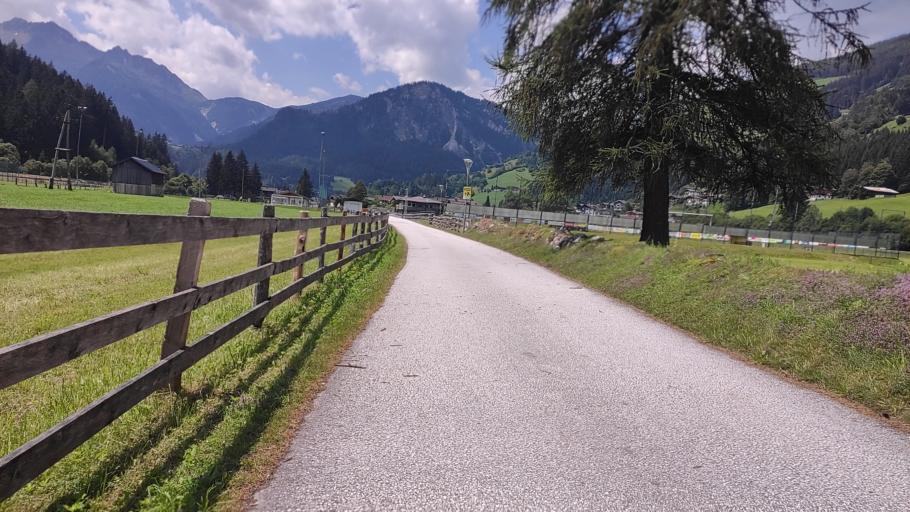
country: AT
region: Salzburg
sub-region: Politischer Bezirk Zell am See
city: Wald im Pinzgau
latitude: 47.2436
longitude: 12.2156
